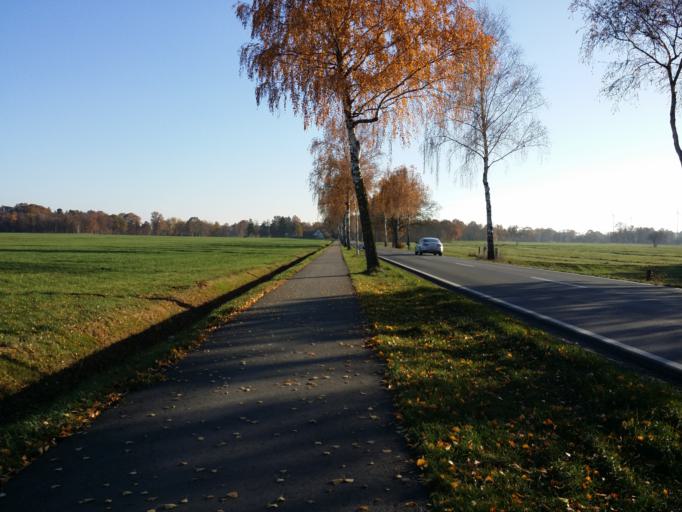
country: DE
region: Lower Saxony
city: Ottersberg
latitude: 53.0458
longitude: 9.1464
